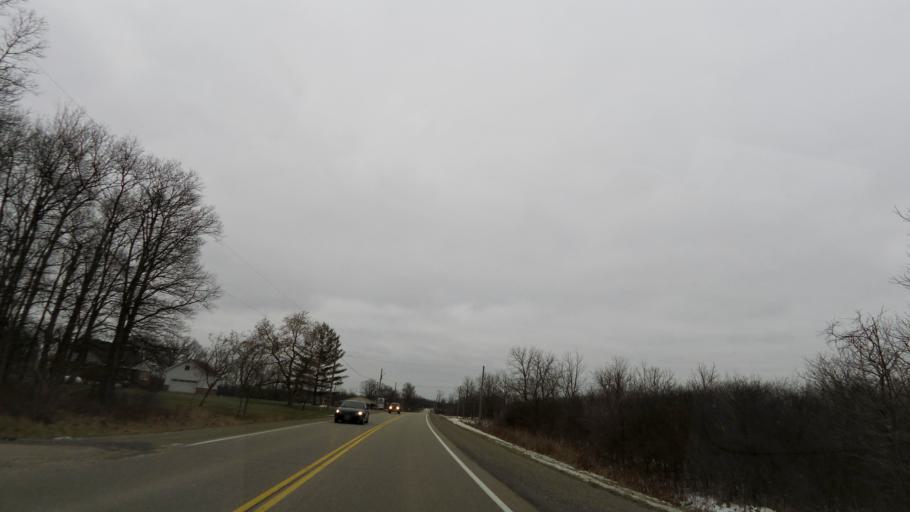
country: CA
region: Ontario
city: Brantford
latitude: 43.1121
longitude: -80.1077
